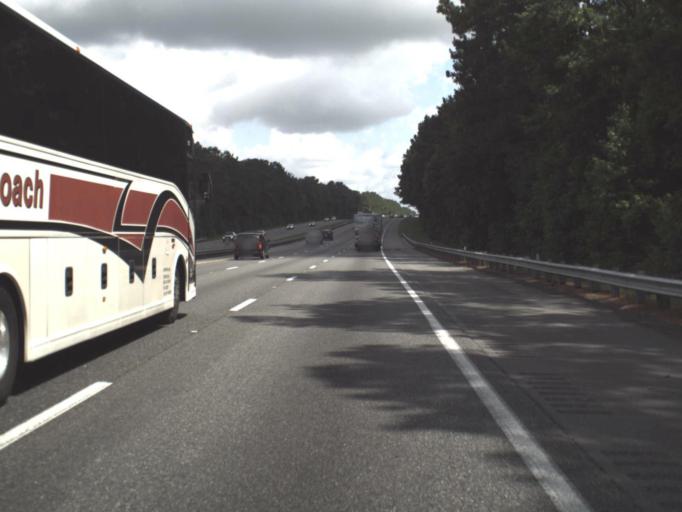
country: US
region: Florida
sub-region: Alachua County
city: High Springs
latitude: 29.9392
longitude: -82.5641
